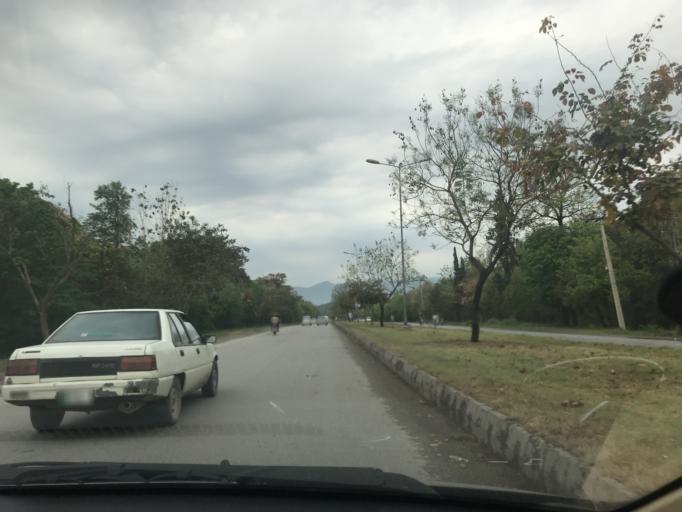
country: PK
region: Islamabad
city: Islamabad
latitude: 33.6802
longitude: 73.1391
